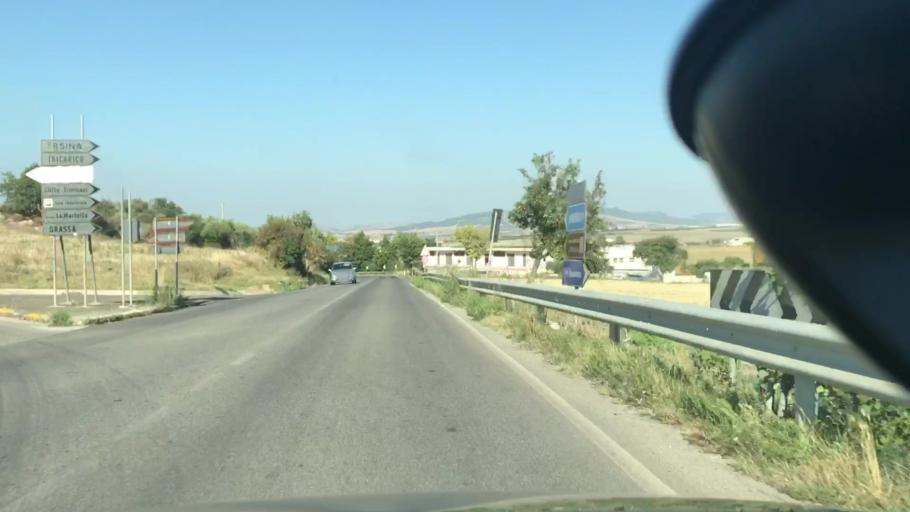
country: IT
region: Basilicate
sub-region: Provincia di Matera
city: La Martella
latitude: 40.6603
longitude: 16.5652
